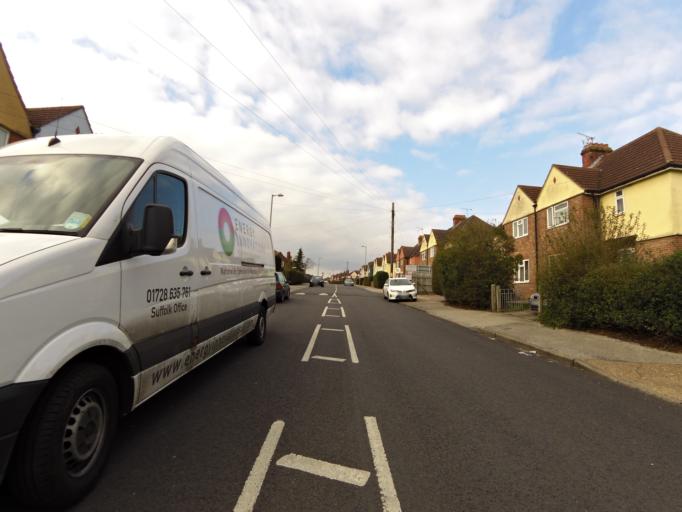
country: GB
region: England
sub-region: Suffolk
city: Bramford
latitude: 52.0804
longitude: 1.1278
